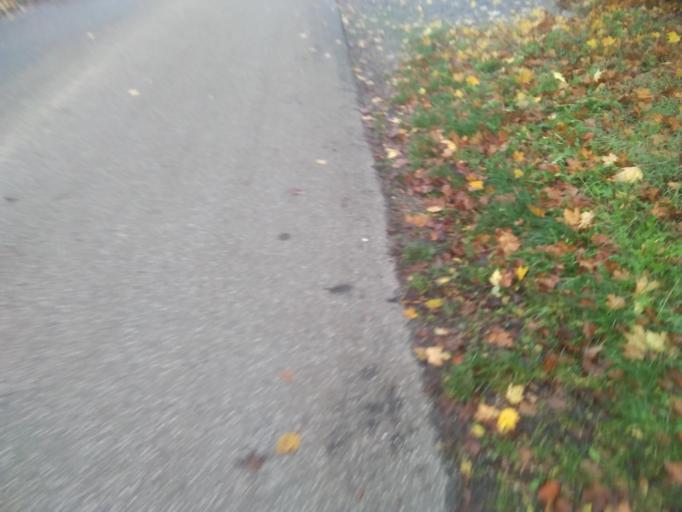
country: DK
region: Capital Region
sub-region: Herlev Kommune
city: Herlev
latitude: 55.7491
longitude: 12.4076
